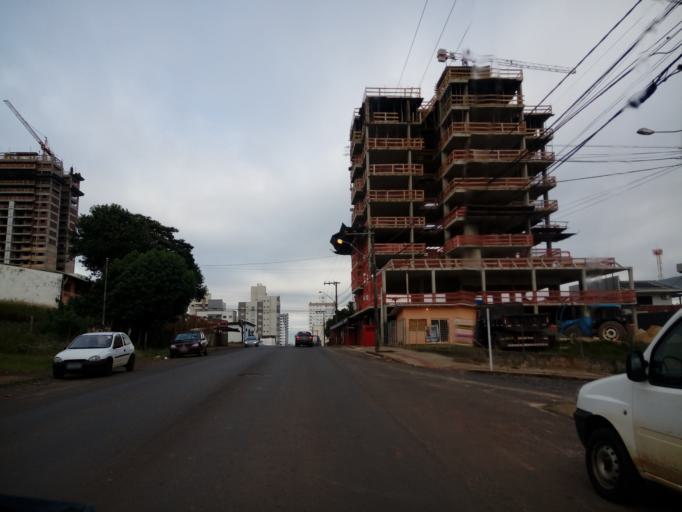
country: BR
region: Santa Catarina
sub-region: Chapeco
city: Chapeco
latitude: -27.0898
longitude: -52.6094
